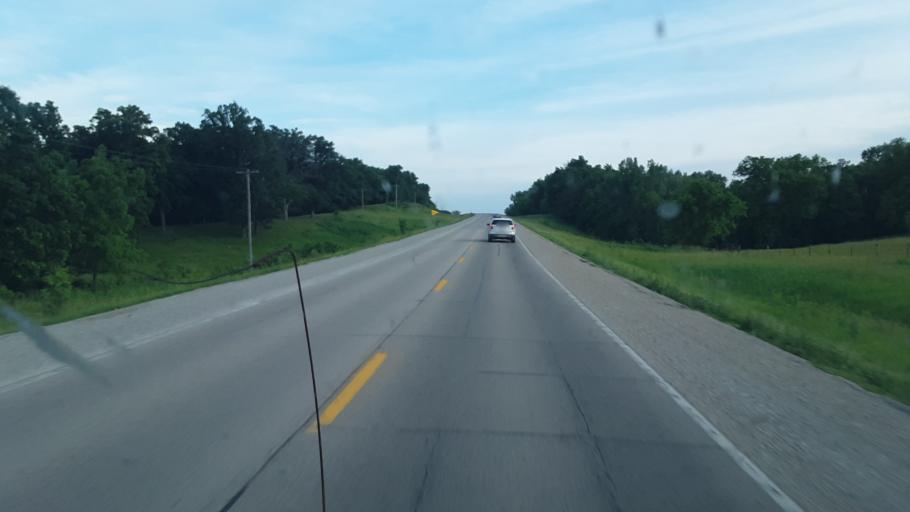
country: US
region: Iowa
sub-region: Benton County
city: Belle Plaine
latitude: 41.8399
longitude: -92.2786
